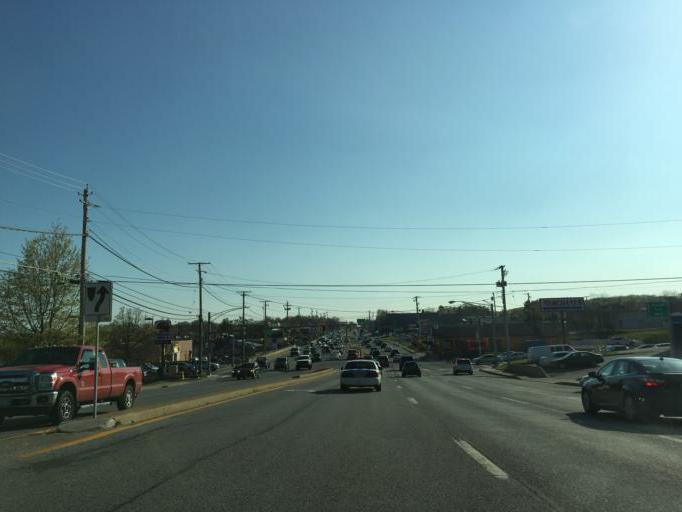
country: US
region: Maryland
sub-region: Baltimore County
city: Overlea
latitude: 39.3750
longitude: -76.5080
